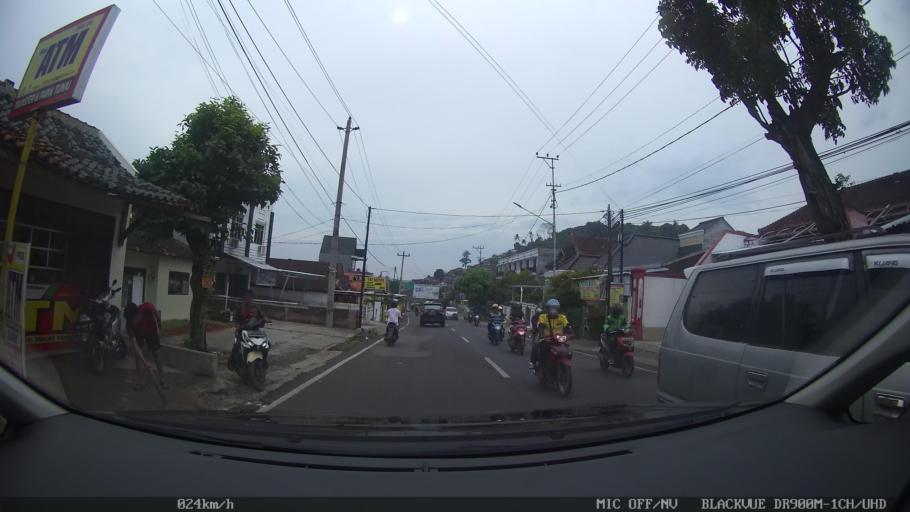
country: ID
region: Lampung
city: Bandarlampung
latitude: -5.4120
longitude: 105.2461
